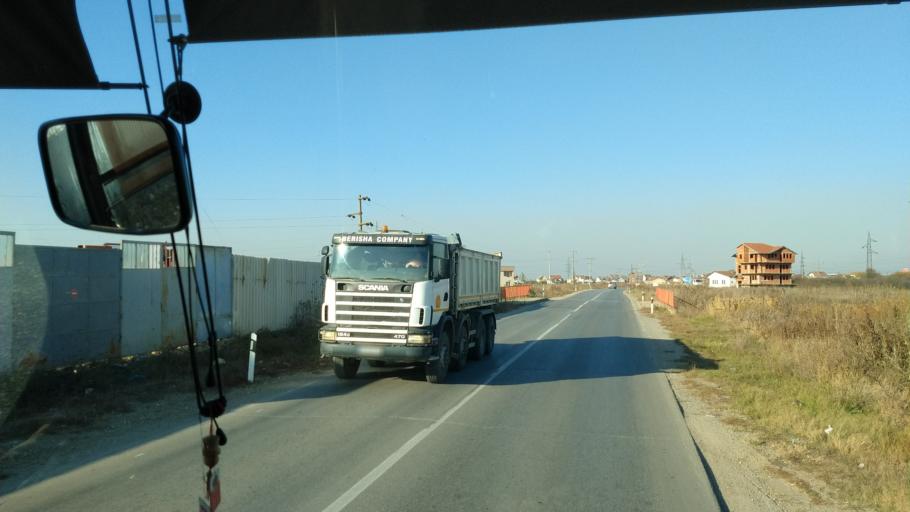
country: XK
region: Pristina
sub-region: Lipjan
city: Lipljan
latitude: 42.5260
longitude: 21.1114
